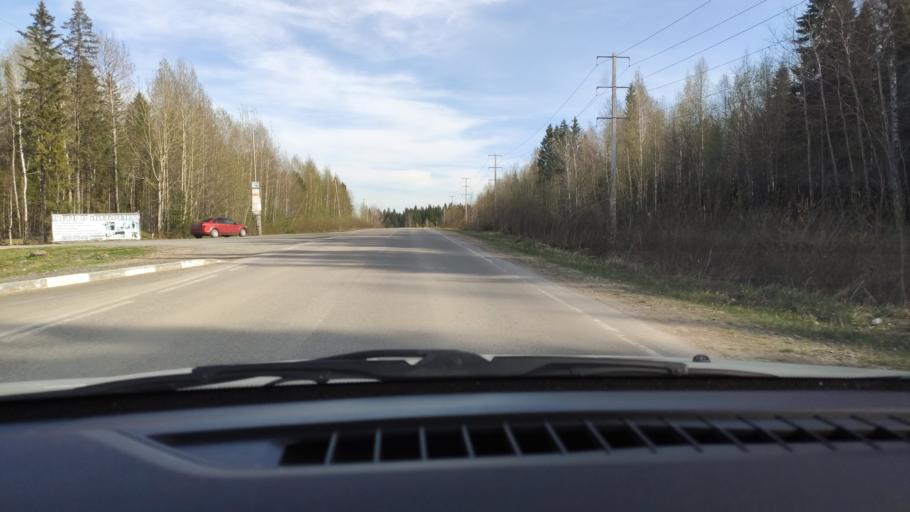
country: RU
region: Perm
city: Novyye Lyady
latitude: 57.9233
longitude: 56.6561
